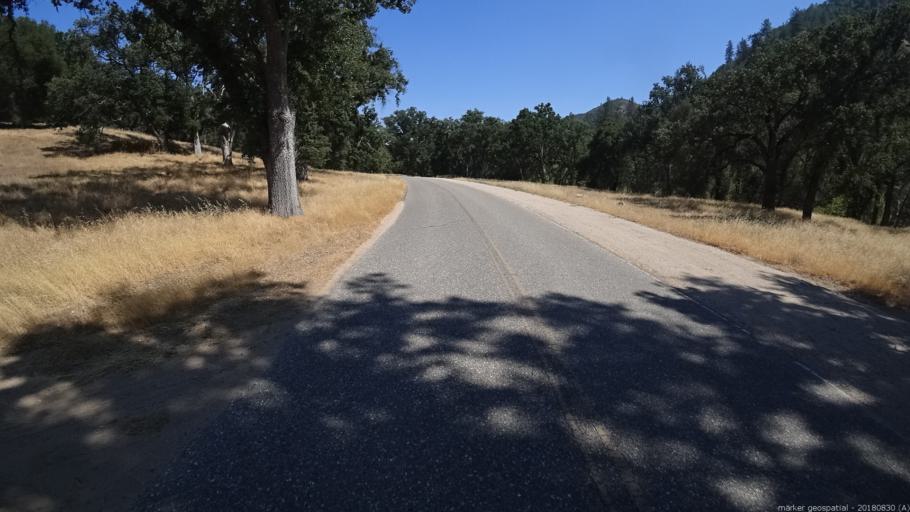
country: US
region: California
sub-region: Monterey County
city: King City
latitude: 36.0720
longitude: -121.3630
